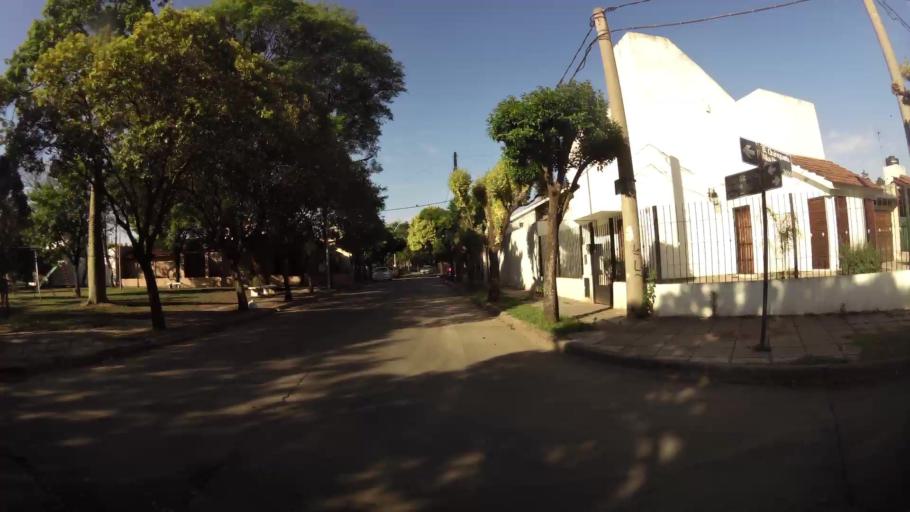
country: AR
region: Cordoba
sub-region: Departamento de Capital
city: Cordoba
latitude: -31.3621
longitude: -64.2230
